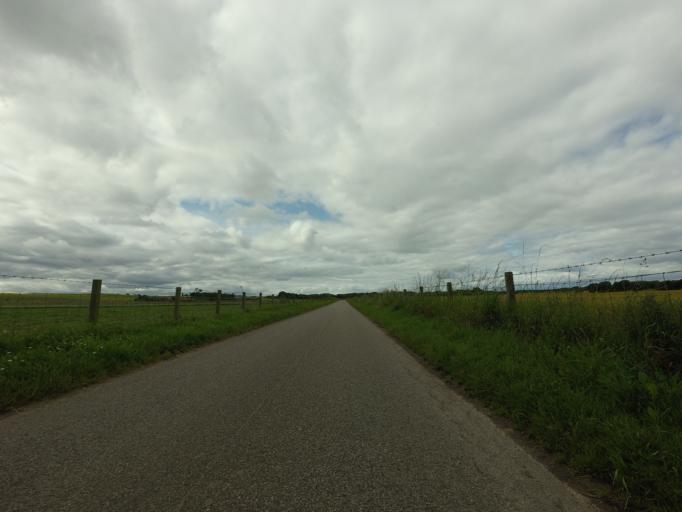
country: GB
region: Scotland
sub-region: Moray
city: Kinloss
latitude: 57.6297
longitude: -3.5428
